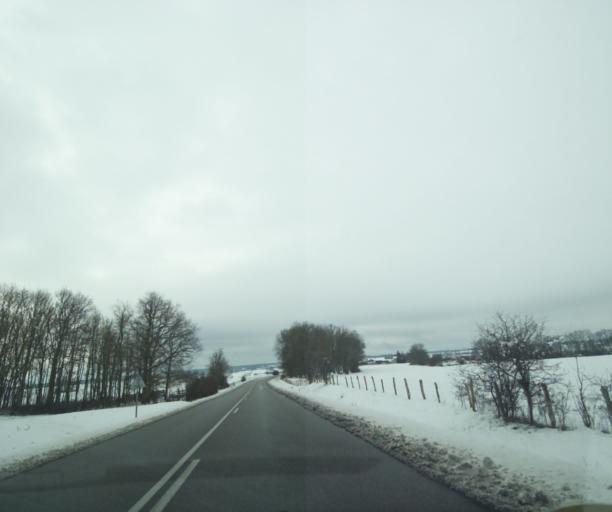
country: FR
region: Champagne-Ardenne
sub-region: Departement de la Haute-Marne
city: Montier-en-Der
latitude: 48.4513
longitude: 4.7402
